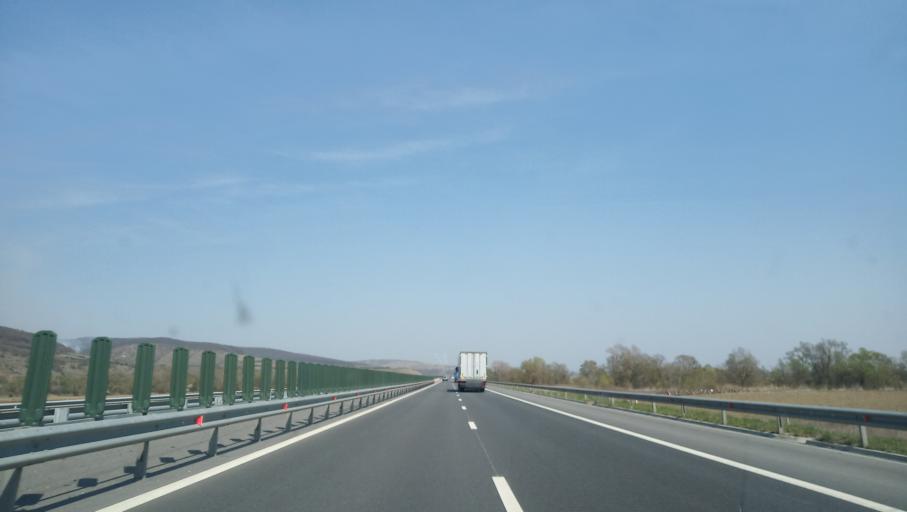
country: RO
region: Alba
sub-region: Comuna Miraslau
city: Miraslau
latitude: 46.3612
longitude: 23.7309
